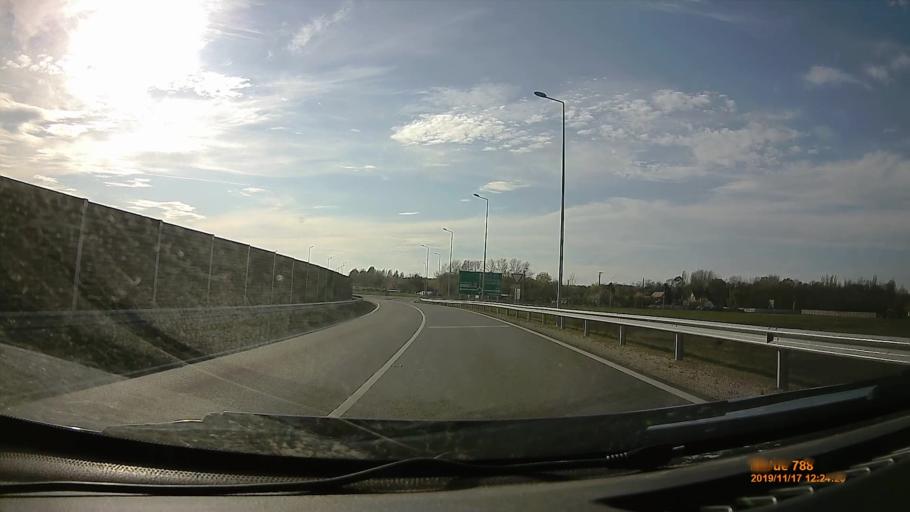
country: HU
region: Bacs-Kiskun
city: Kecskemet
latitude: 46.9368
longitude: 19.6420
